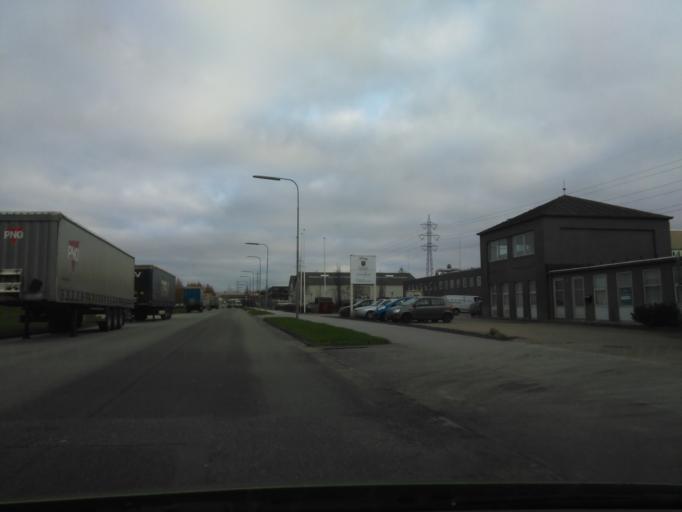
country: DK
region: Central Jutland
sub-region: Arhus Kommune
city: Stavtrup
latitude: 56.1672
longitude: 10.1112
